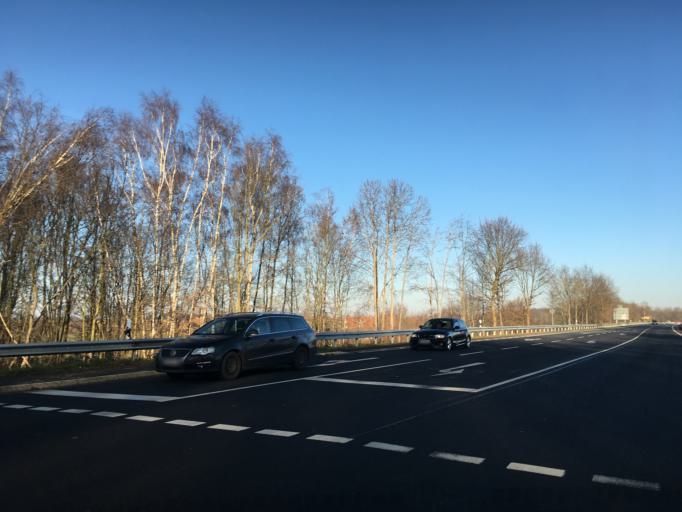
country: DE
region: North Rhine-Westphalia
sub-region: Regierungsbezirk Munster
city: Muenster
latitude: 51.9885
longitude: 7.5399
